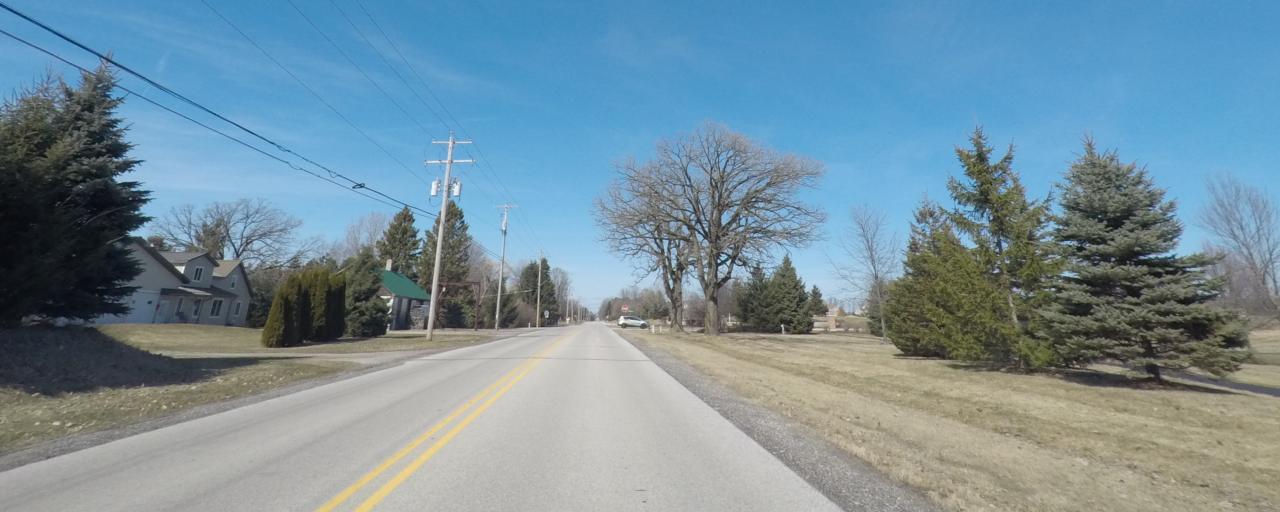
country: US
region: Wisconsin
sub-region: Waukesha County
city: Merton
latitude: 43.1296
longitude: -88.3275
